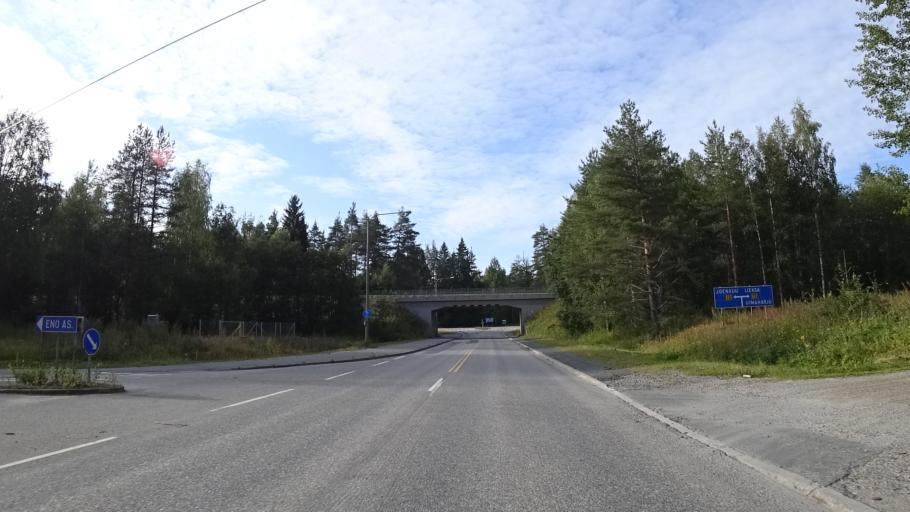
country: FI
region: North Karelia
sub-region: Joensuu
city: Eno
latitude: 62.8069
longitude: 30.1516
